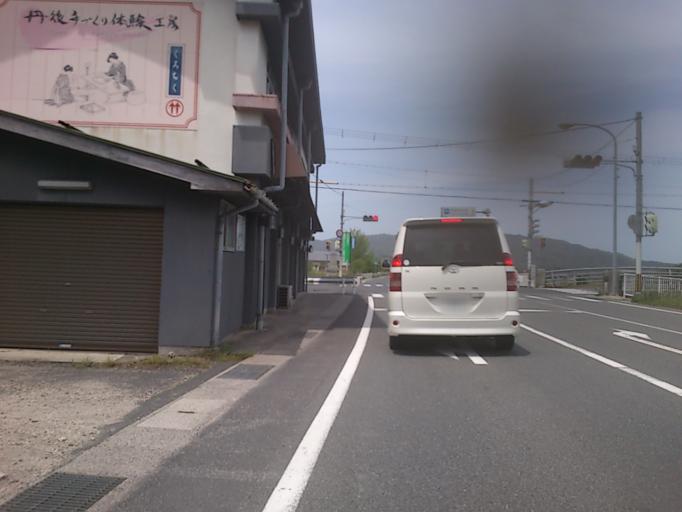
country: JP
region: Kyoto
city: Miyazu
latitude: 35.6590
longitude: 135.0872
